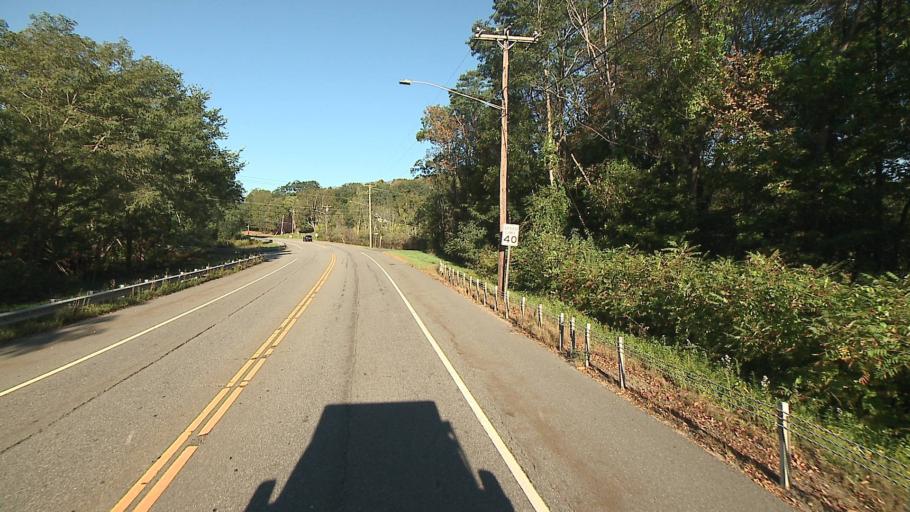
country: US
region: Connecticut
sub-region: Litchfield County
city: Torrington
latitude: 41.7861
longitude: -73.1429
